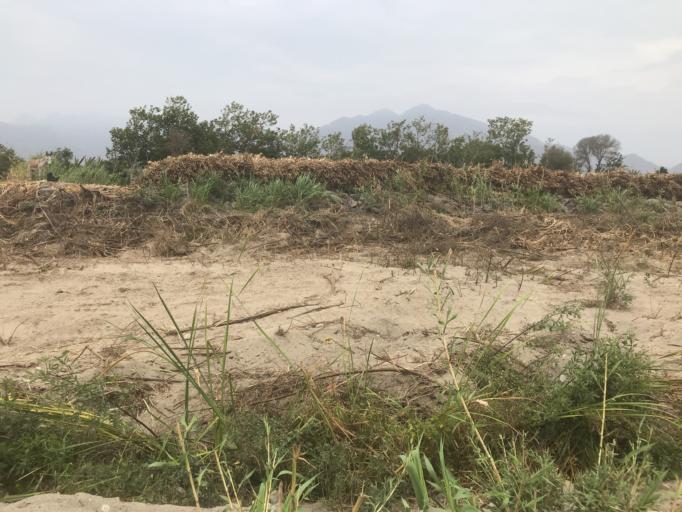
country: PE
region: La Libertad
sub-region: Viru
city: Viru
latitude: -8.4228
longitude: -78.7922
